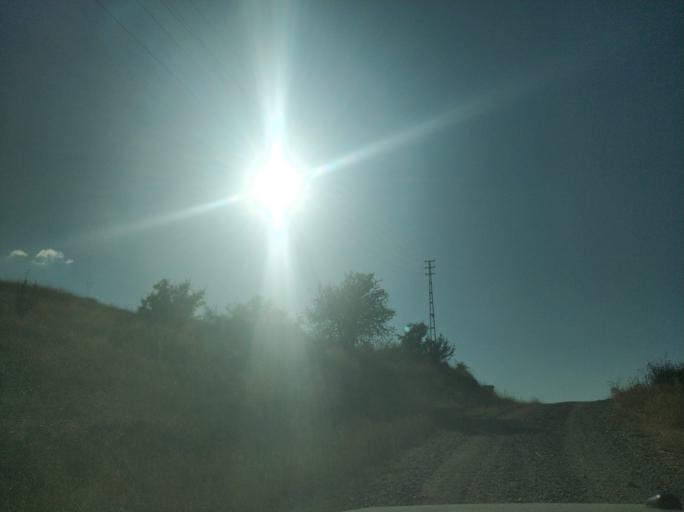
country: TR
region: Sivas
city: Zara
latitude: 39.8284
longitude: 37.8991
